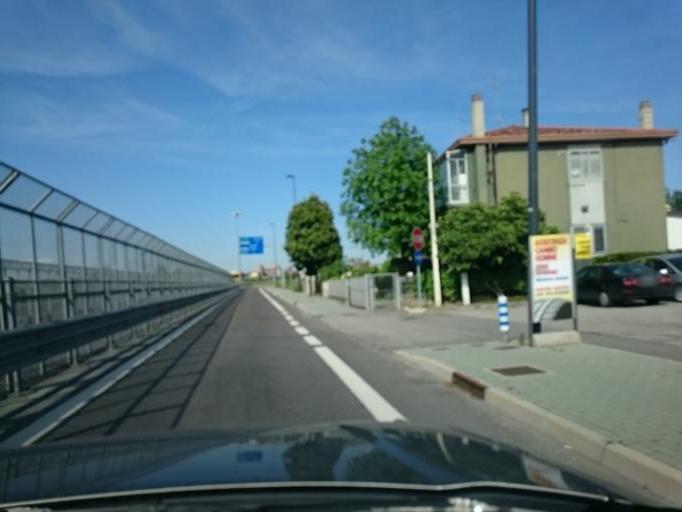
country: IT
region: Veneto
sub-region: Provincia di Venezia
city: Campalto
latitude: 45.4809
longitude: 12.2722
